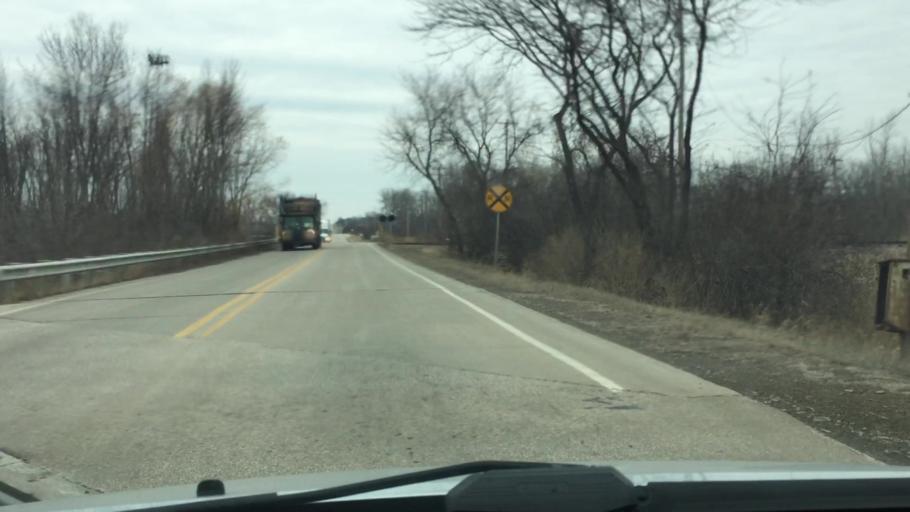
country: US
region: Wisconsin
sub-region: Waukesha County
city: Menomonee Falls
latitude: 43.1900
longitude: -88.0633
